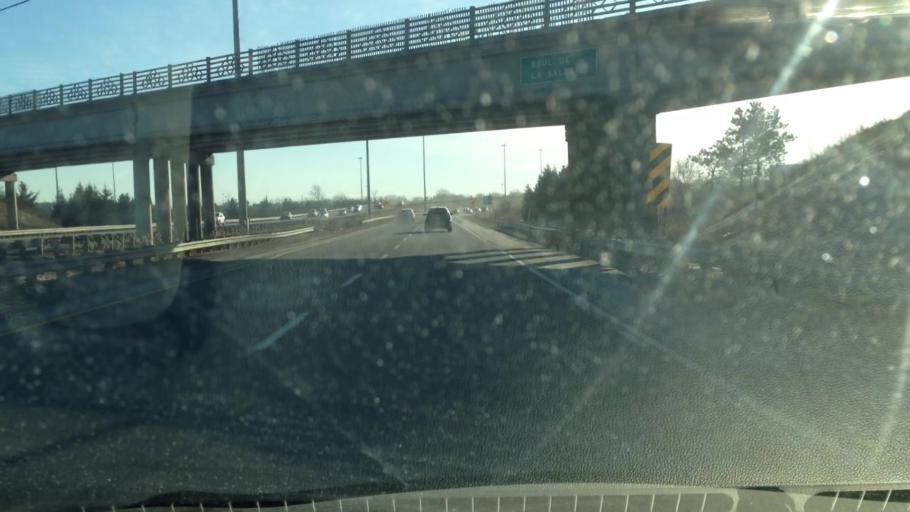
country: CA
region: Quebec
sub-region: Laurentides
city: Saint-Jerome
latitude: 45.7964
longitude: -74.0260
